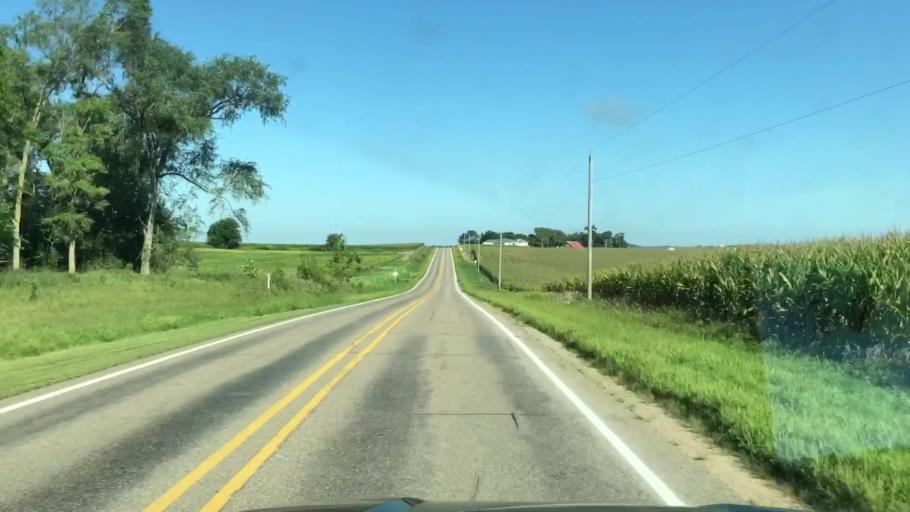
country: US
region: Iowa
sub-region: Woodbury County
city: Sergeant Bluff
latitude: 42.4267
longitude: -96.2794
